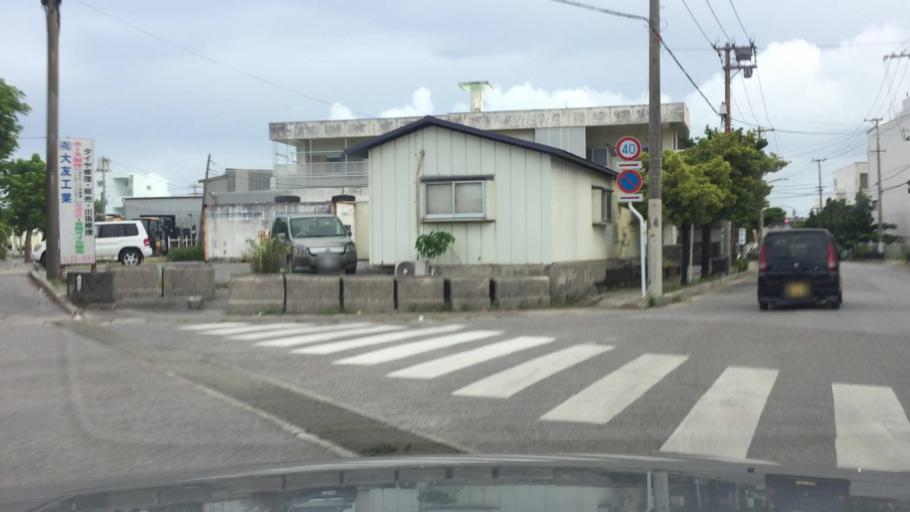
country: JP
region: Okinawa
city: Ishigaki
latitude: 24.3496
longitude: 124.1587
